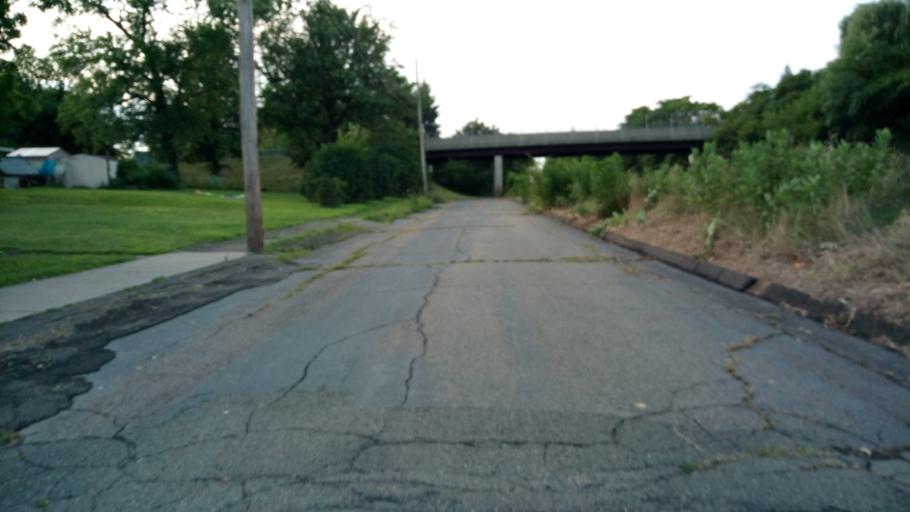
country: US
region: New York
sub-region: Chemung County
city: Elmira
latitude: 42.0989
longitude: -76.8112
